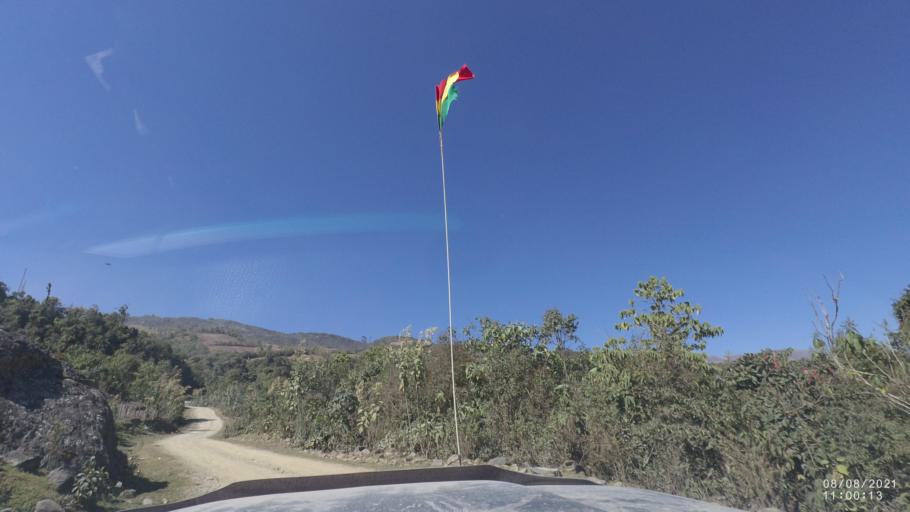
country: BO
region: Cochabamba
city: Colchani
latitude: -16.7486
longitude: -66.6882
